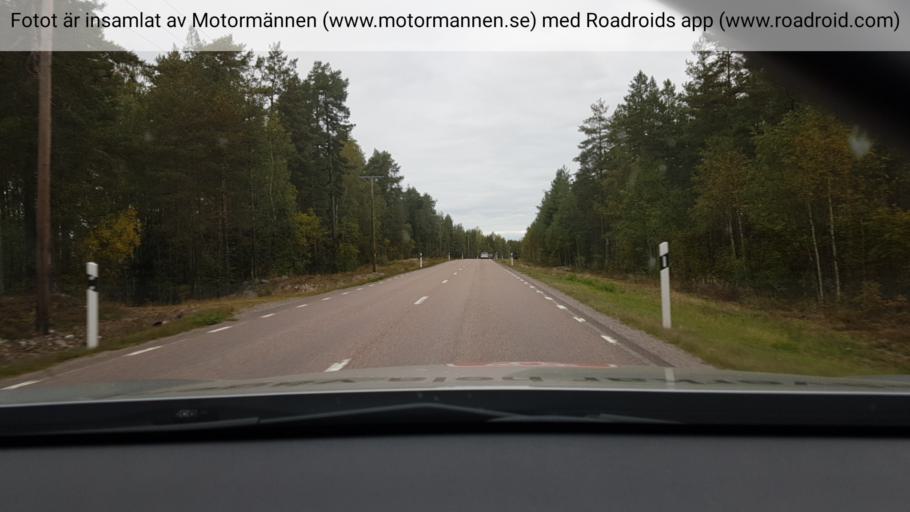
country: SE
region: Gaevleborg
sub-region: Gavle Kommun
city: Valbo
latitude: 60.5607
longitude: 16.9513
